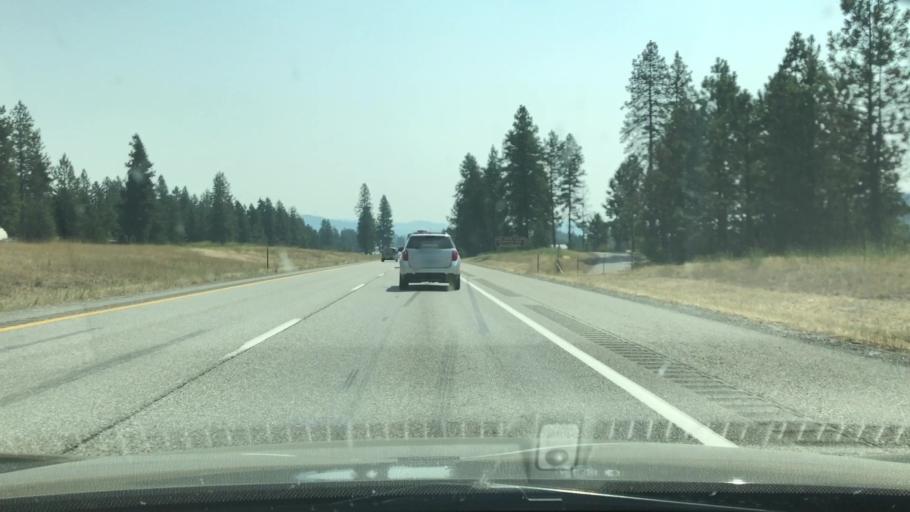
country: US
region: Idaho
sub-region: Kootenai County
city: Coeur d'Alene
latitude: 47.7051
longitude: -116.8405
